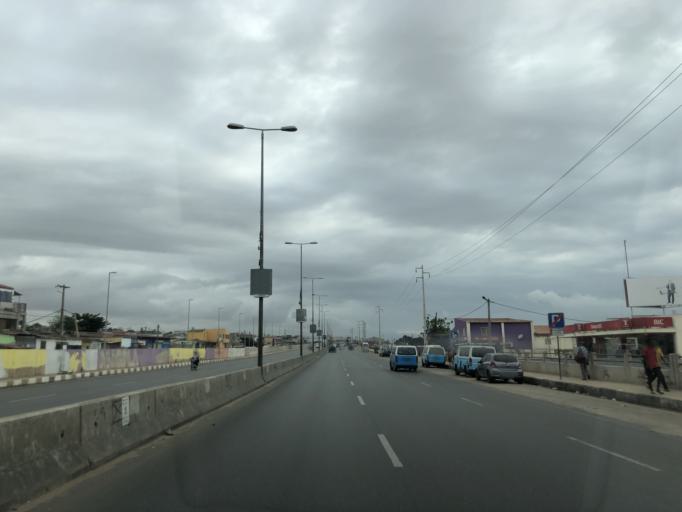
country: AO
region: Luanda
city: Luanda
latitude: -8.8567
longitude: 13.2181
